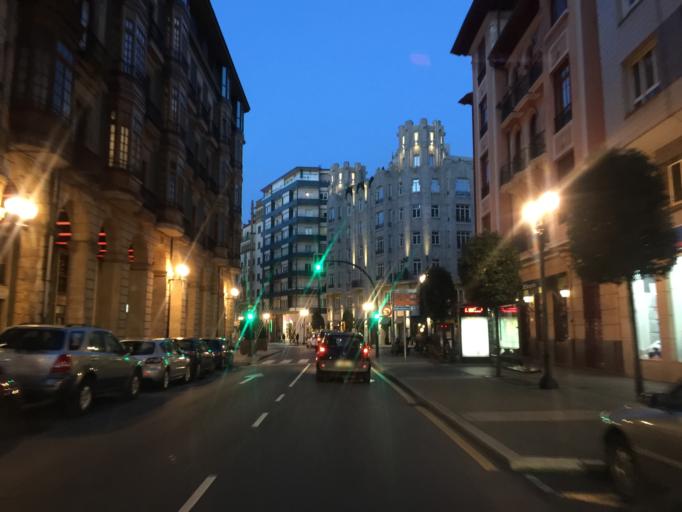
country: ES
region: Asturias
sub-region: Province of Asturias
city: Gijon
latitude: 43.5419
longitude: -5.6680
